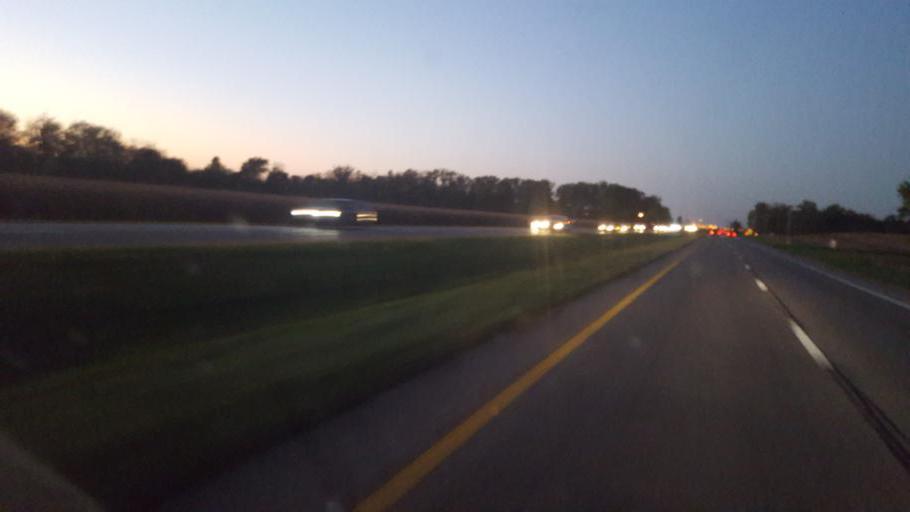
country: US
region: Ohio
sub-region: Pickaway County
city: Logan Elm Village
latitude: 39.5270
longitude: -82.9676
